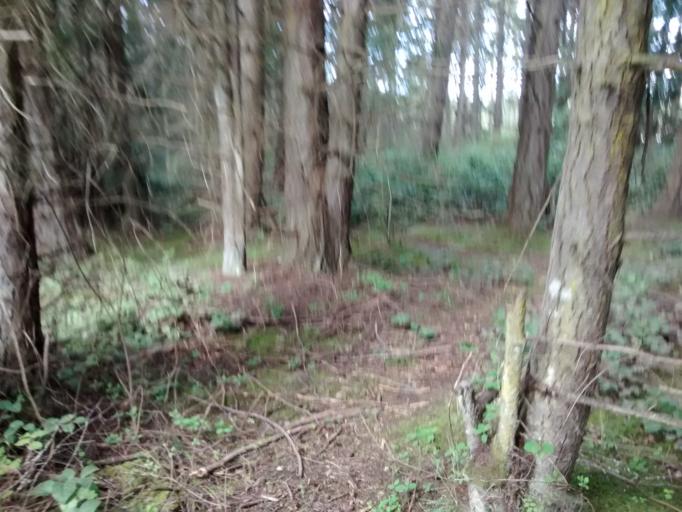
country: US
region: Washington
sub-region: Clallam County
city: Port Angeles
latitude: 48.1190
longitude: -123.4805
